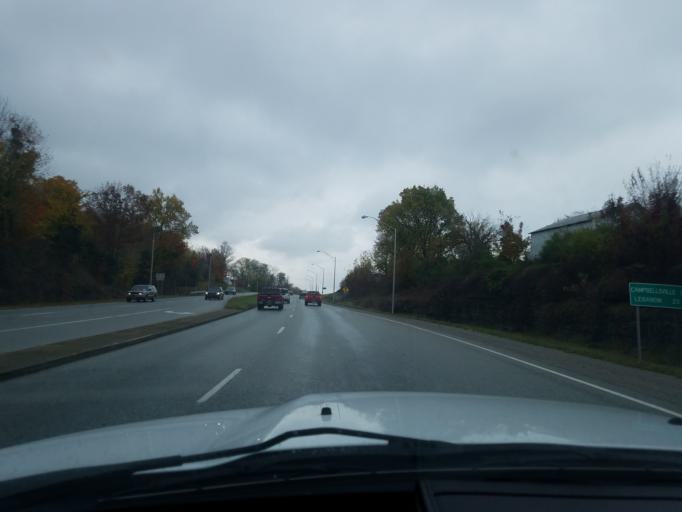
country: US
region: Kentucky
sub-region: Taylor County
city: Campbellsville
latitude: 37.3383
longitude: -85.3593
